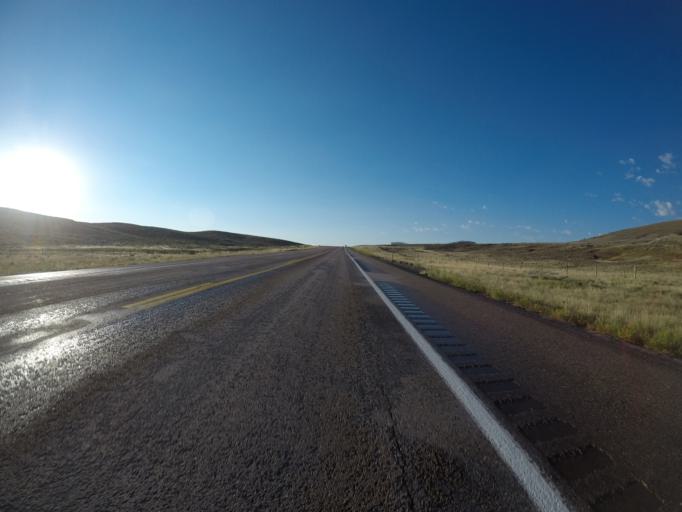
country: US
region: Wyoming
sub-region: Lincoln County
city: Kemmerer
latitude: 41.8719
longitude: -110.4772
